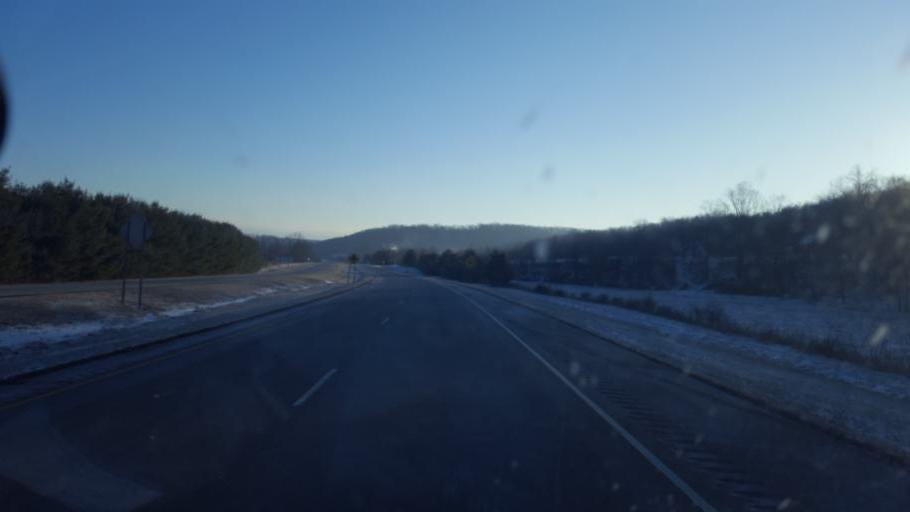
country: US
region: Ohio
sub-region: Pike County
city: Piketon
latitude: 39.0419
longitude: -83.1616
